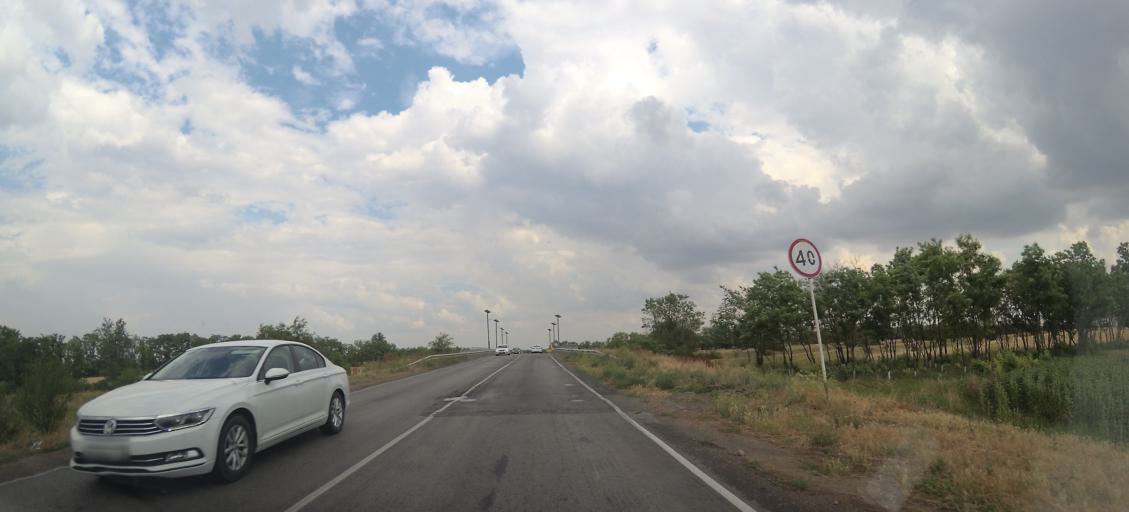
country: RU
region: Rostov
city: Letnik
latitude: 46.0869
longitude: 41.1854
